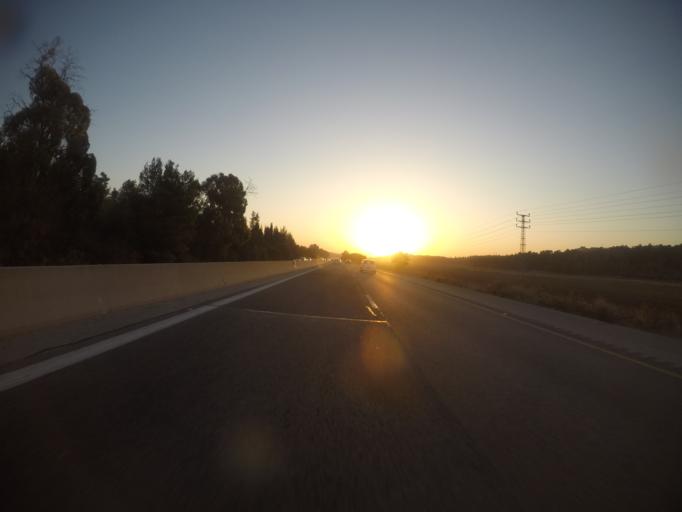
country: PS
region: West Bank
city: Barta`ah ash Sharqiyah
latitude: 32.4930
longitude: 35.0562
